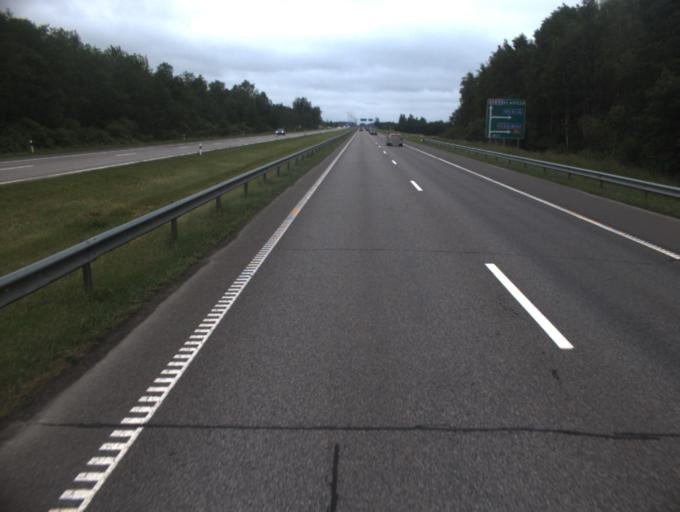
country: LT
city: Vilkija
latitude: 55.1331
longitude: 23.7345
